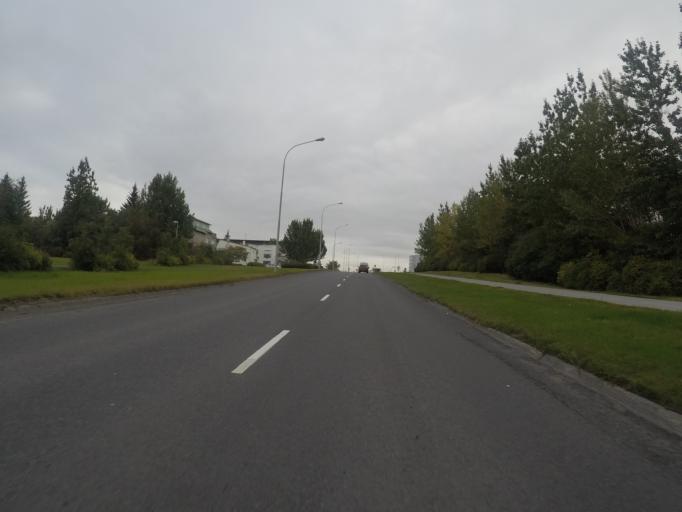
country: IS
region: Capital Region
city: Reykjavik
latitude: 64.1483
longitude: -21.8741
